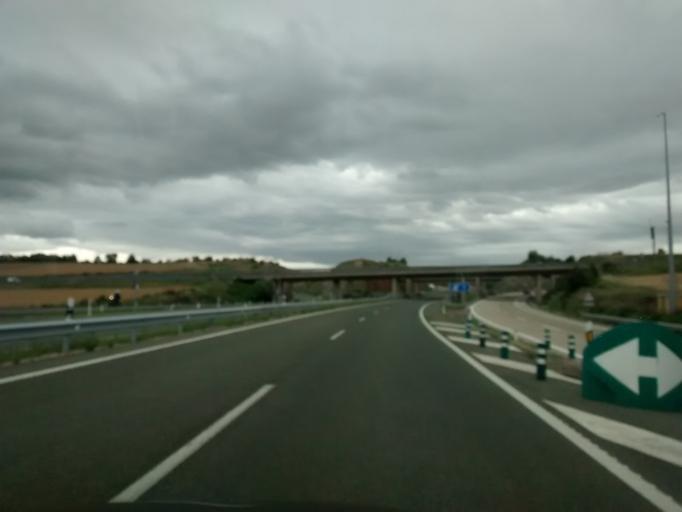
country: ES
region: Basque Country
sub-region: Provincia de Alava
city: Arminon
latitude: 42.7120
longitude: -2.9042
